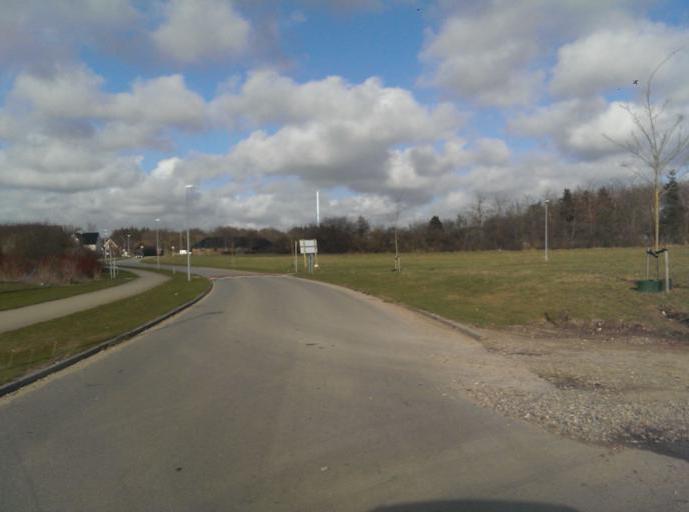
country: DK
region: South Denmark
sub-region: Esbjerg Kommune
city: Bramming
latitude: 55.4594
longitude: 8.7064
